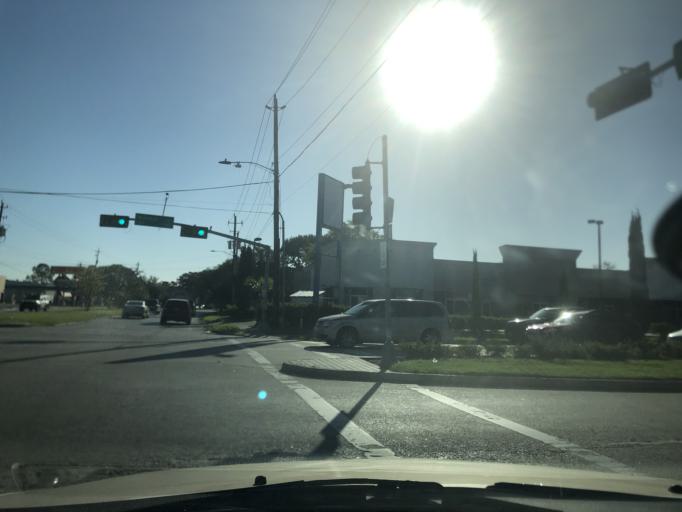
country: US
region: Texas
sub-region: Harris County
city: Bunker Hill Village
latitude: 29.7479
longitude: -95.5722
